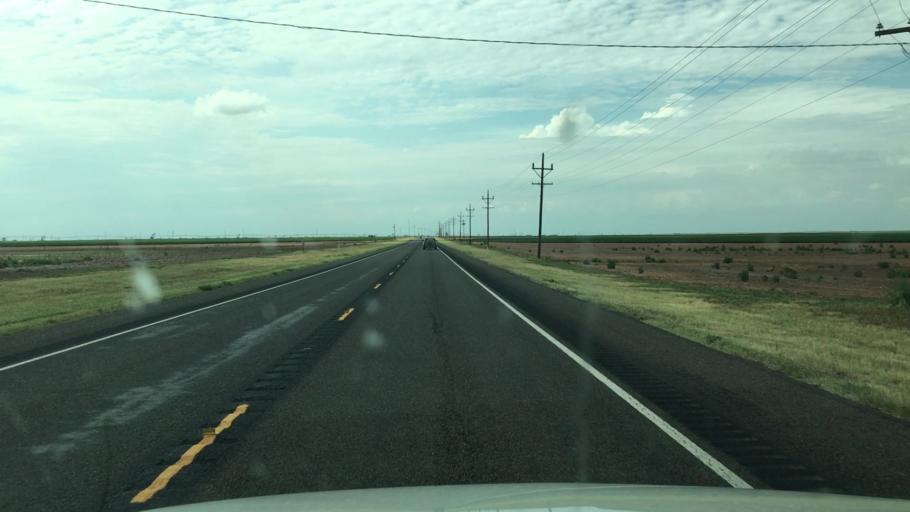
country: US
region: Texas
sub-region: Dawson County
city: Lamesa
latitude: 32.8833
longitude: -102.0831
